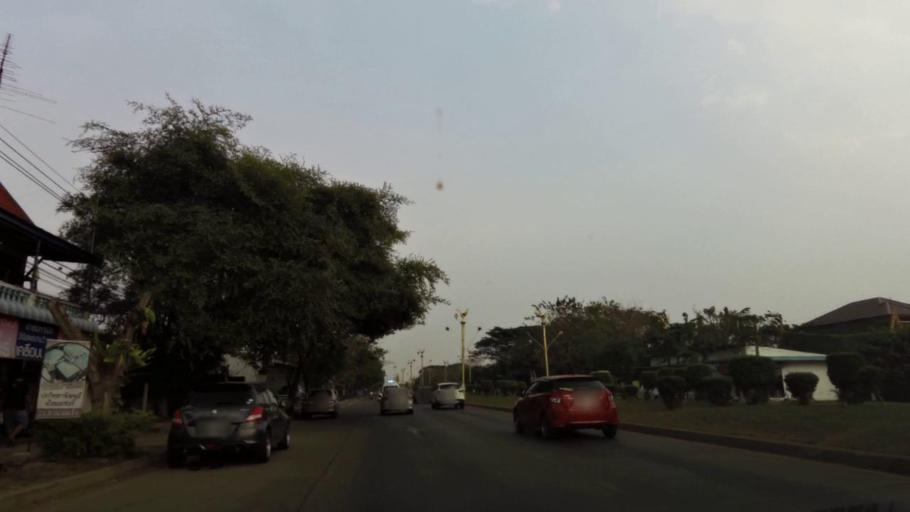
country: TH
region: Phra Nakhon Si Ayutthaya
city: Phra Nakhon Si Ayutthaya
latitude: 14.3510
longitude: 100.5711
